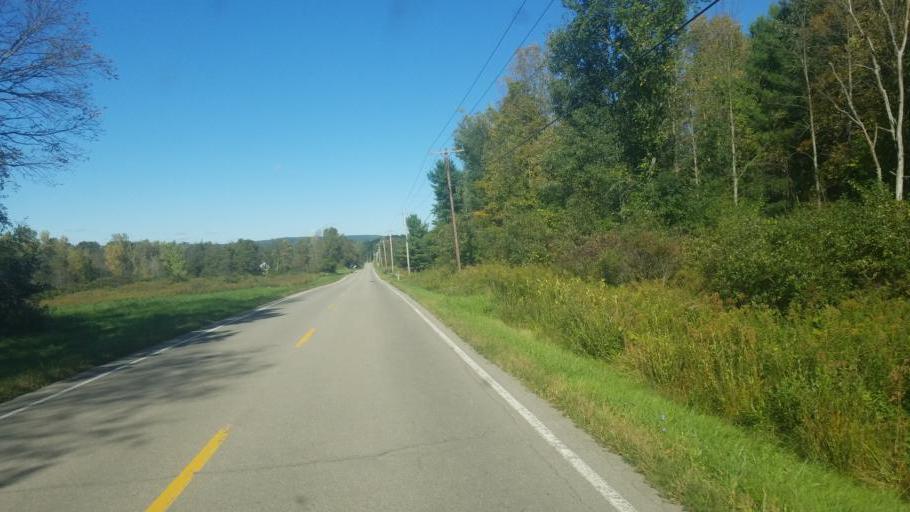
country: US
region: New York
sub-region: Allegany County
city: Friendship
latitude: 42.3024
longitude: -78.1117
